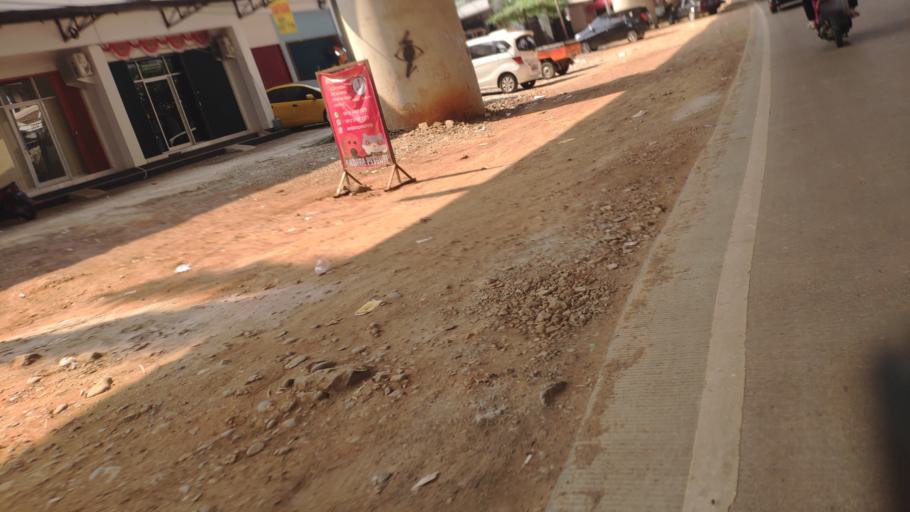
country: ID
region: West Java
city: Pamulang
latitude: -6.3146
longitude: 106.8038
